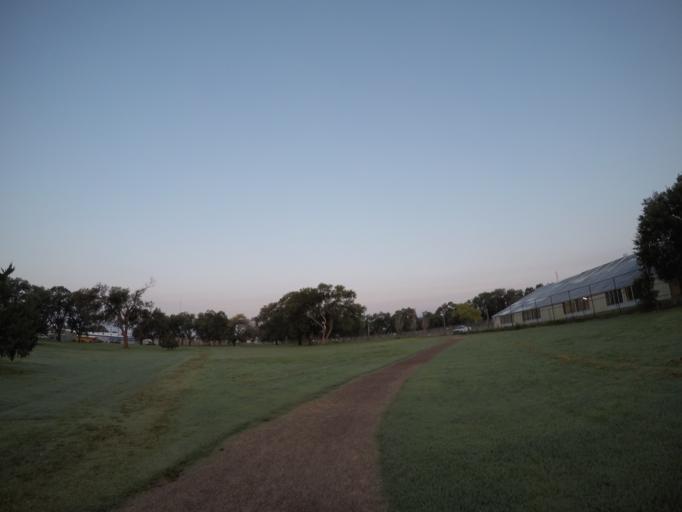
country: US
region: New Mexico
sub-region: Curry County
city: Clovis
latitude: 34.4057
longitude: -103.1840
